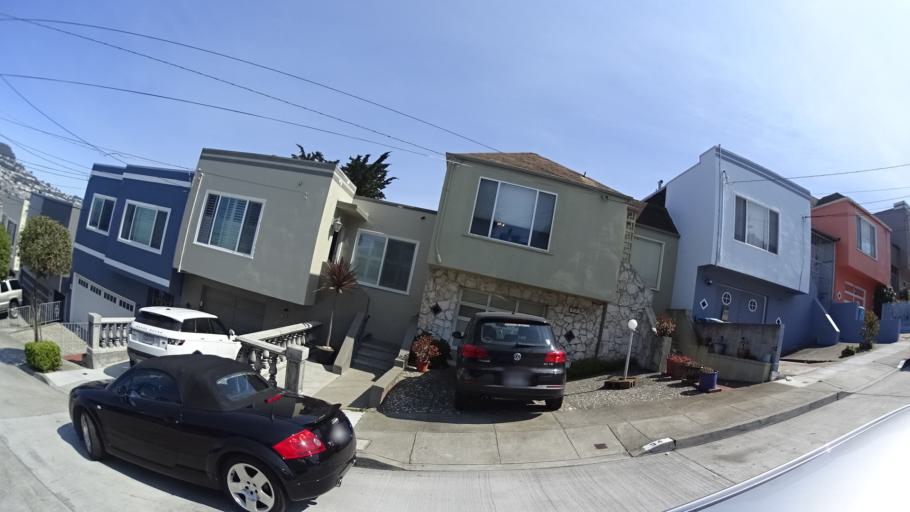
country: US
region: California
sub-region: San Mateo County
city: Daly City
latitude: 37.7190
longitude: -122.4612
